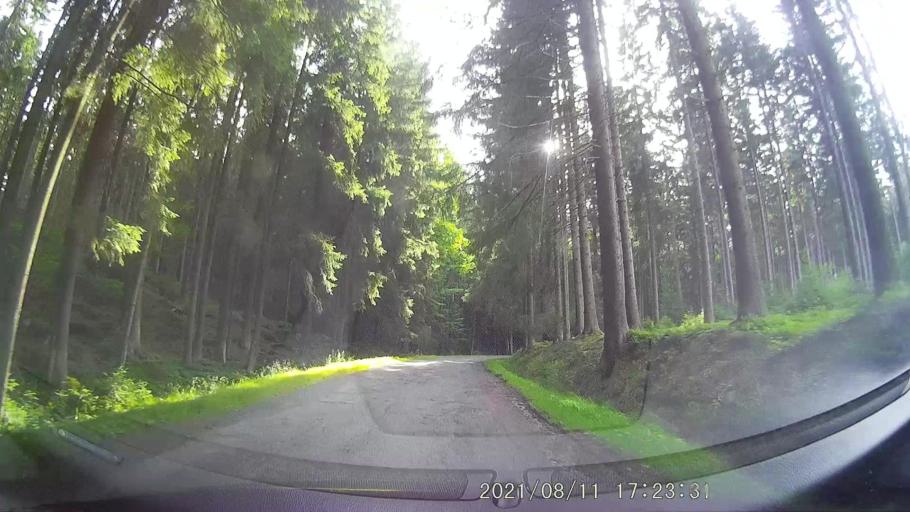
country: PL
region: Lower Silesian Voivodeship
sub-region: Powiat klodzki
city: Polanica-Zdroj
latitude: 50.3039
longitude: 16.5021
